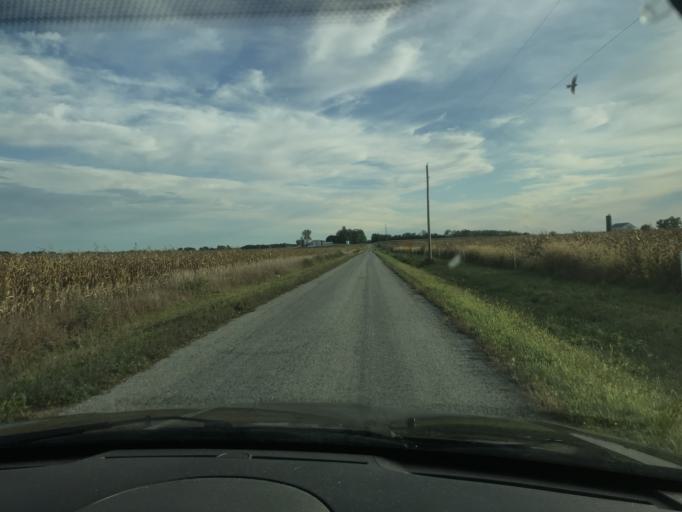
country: US
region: Ohio
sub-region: Logan County
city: West Liberty
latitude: 40.2135
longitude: -83.8081
